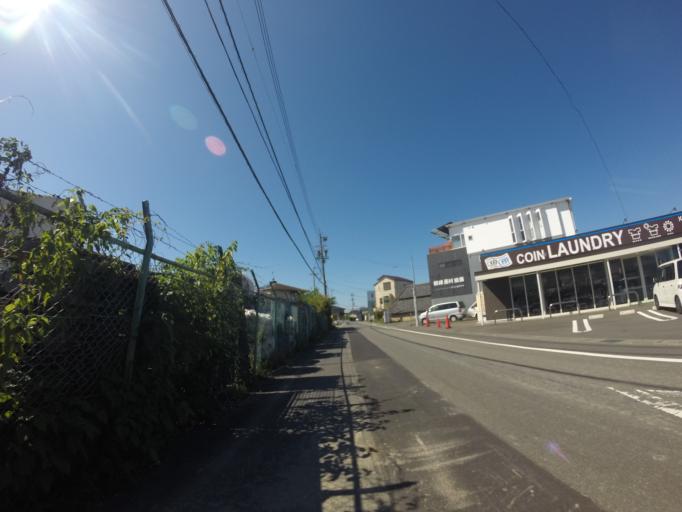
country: JP
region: Shizuoka
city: Fujieda
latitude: 34.8546
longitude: 138.2625
